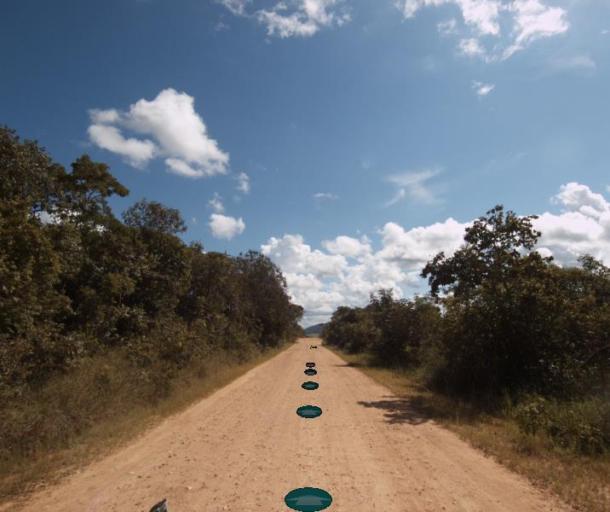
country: BR
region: Goias
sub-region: Pirenopolis
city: Pirenopolis
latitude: -15.7864
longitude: -49.0621
